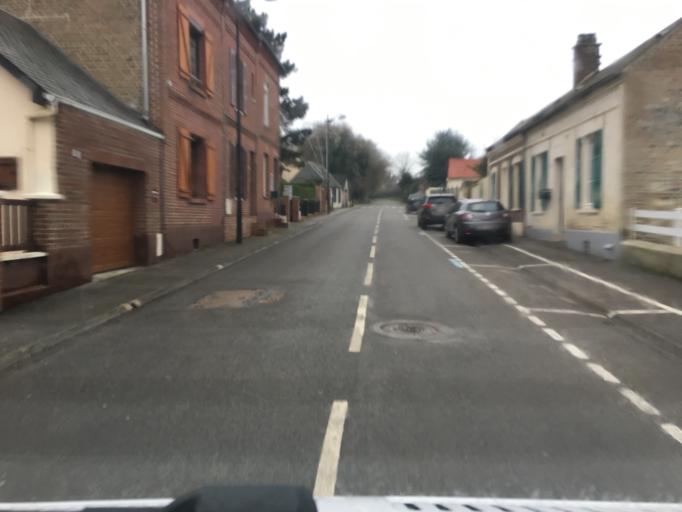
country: FR
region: Picardie
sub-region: Departement de la Somme
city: Saint-Valery-sur-Somme
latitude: 50.1774
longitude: 1.6428
